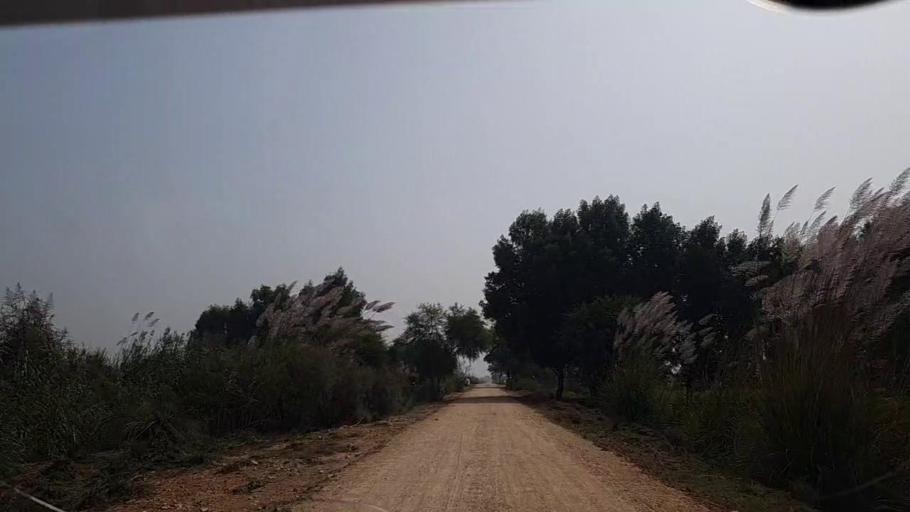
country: PK
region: Sindh
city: Garhi Yasin
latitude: 27.9305
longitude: 68.5580
